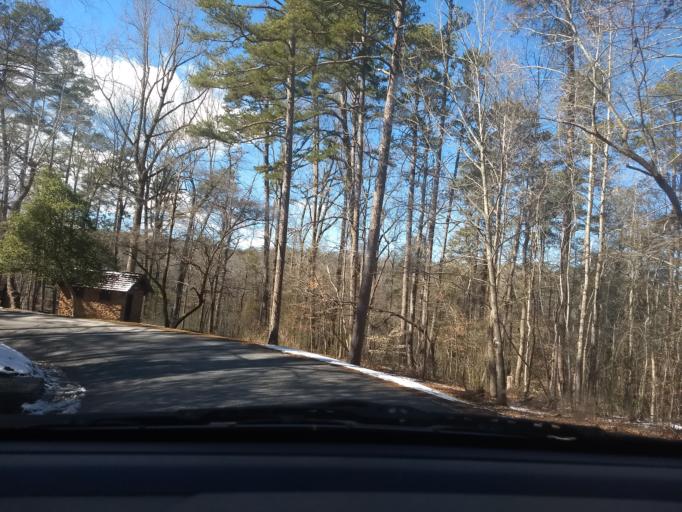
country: US
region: South Carolina
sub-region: Greenville County
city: Wade Hampton
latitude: 34.9273
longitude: -82.3661
